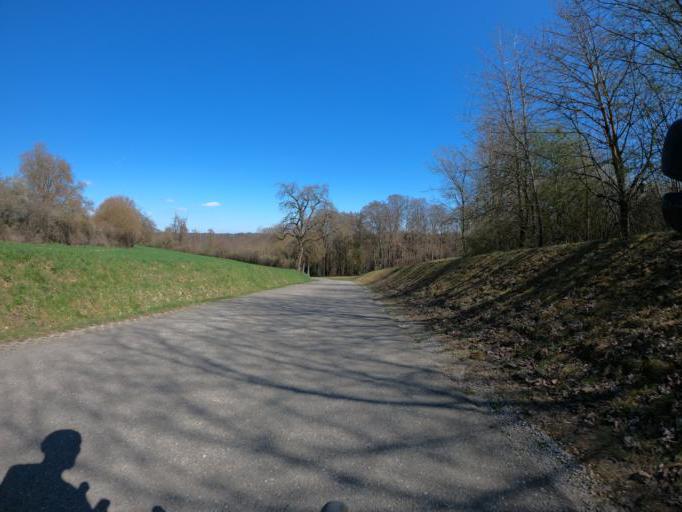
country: DE
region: Baden-Wuerttemberg
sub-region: Karlsruhe Region
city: Empfingen
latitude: 48.4001
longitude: 8.7587
